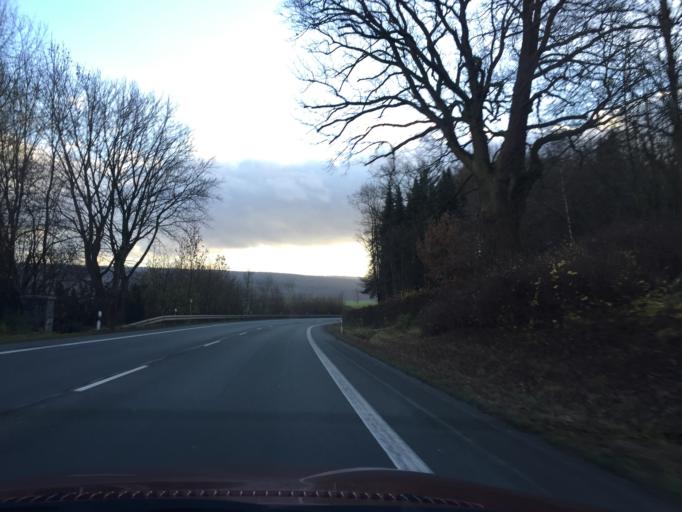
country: DE
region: North Rhine-Westphalia
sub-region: Regierungsbezirk Detmold
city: Hoexter
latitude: 51.8047
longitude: 9.4024
